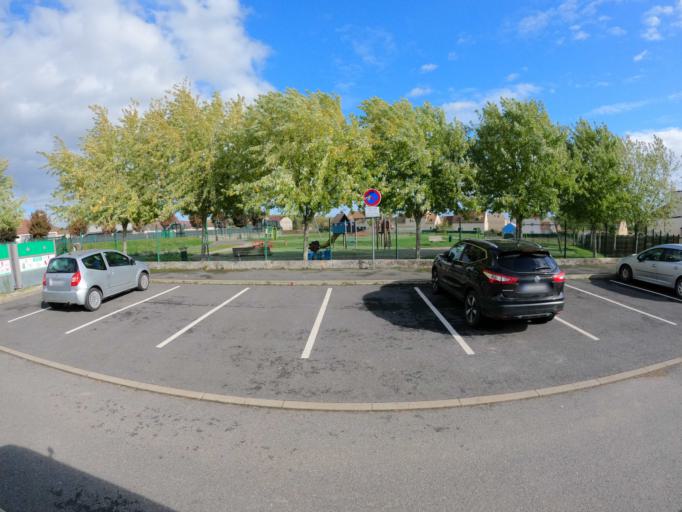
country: FR
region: Ile-de-France
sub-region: Departement de Seine-et-Marne
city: Montry
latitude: 48.8834
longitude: 2.8327
